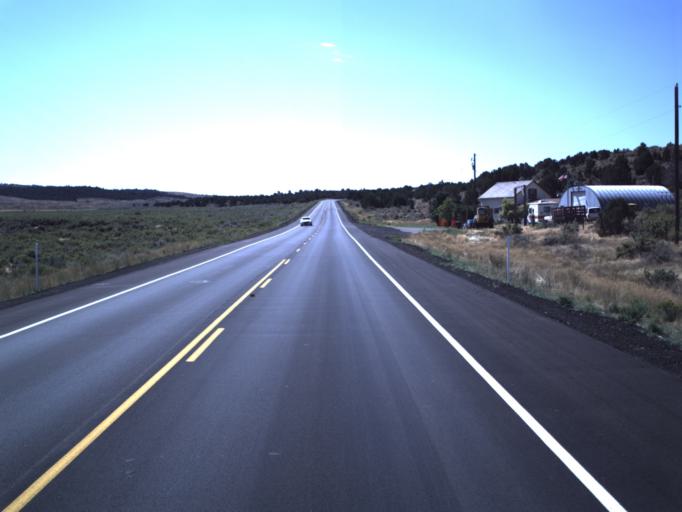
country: US
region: Utah
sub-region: Utah County
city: Eagle Mountain
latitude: 40.0175
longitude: -112.2790
